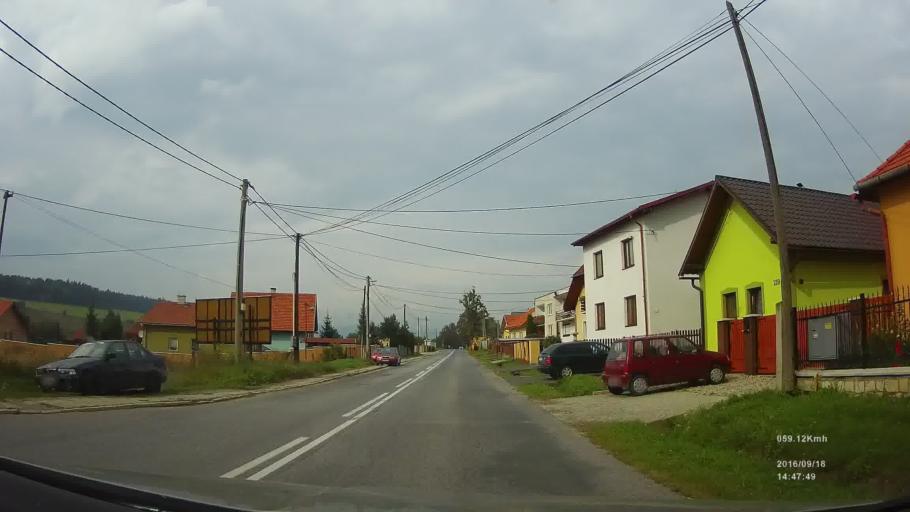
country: SK
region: Kosicky
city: Spisska Nova Ves
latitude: 48.9695
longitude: 20.5825
